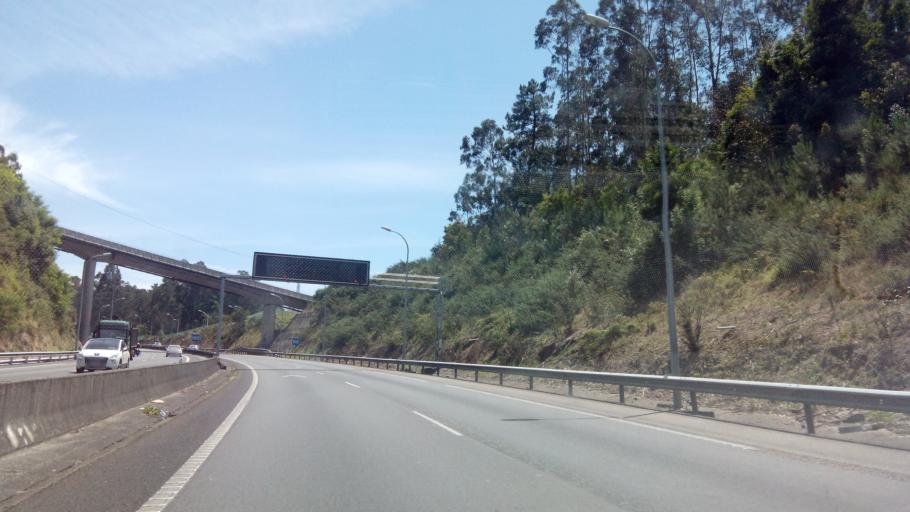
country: ES
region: Galicia
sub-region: Provincia de Pontevedra
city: Vigo
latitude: 42.2432
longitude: -8.6820
